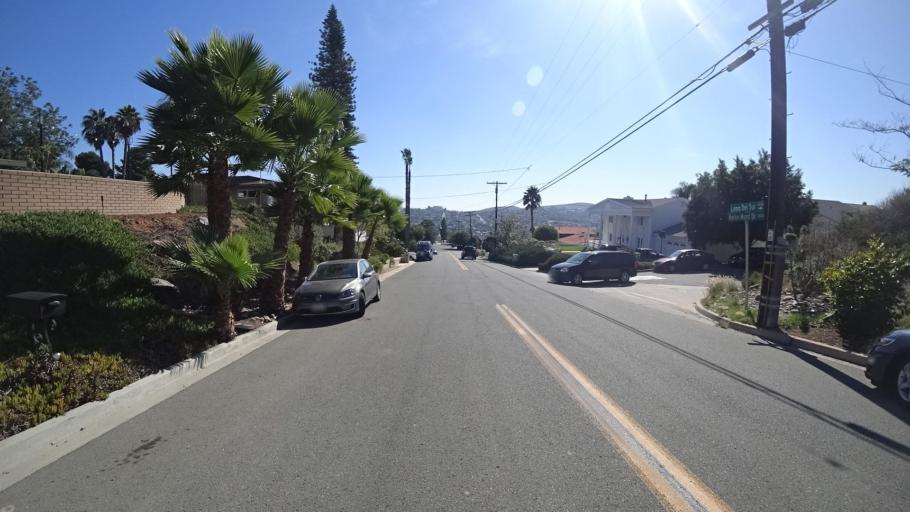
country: US
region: California
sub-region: San Diego County
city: Casa de Oro-Mount Helix
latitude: 32.7567
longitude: -116.9791
